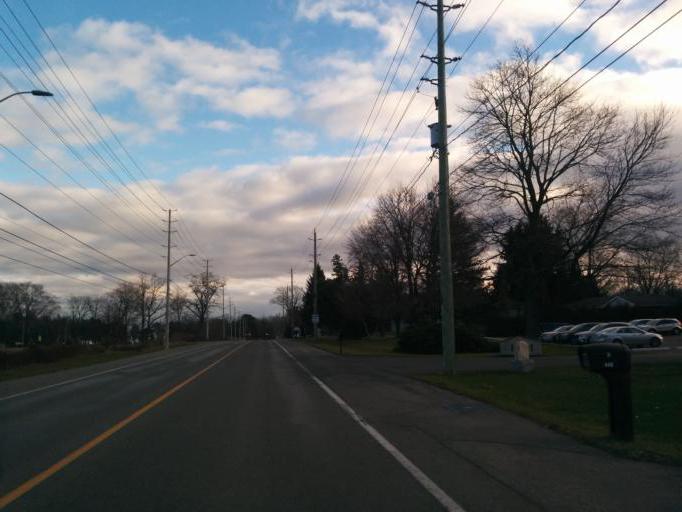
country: CA
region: Ontario
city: Oakville
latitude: 43.4860
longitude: -79.6313
